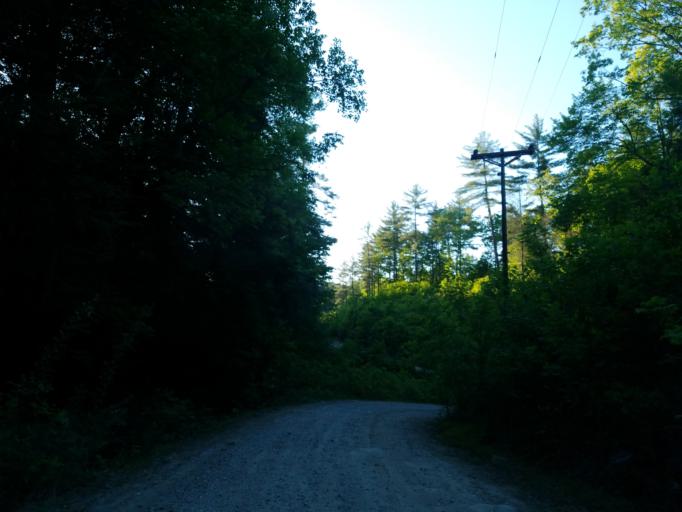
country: US
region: Georgia
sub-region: Fannin County
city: Blue Ridge
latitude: 34.7079
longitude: -84.1492
